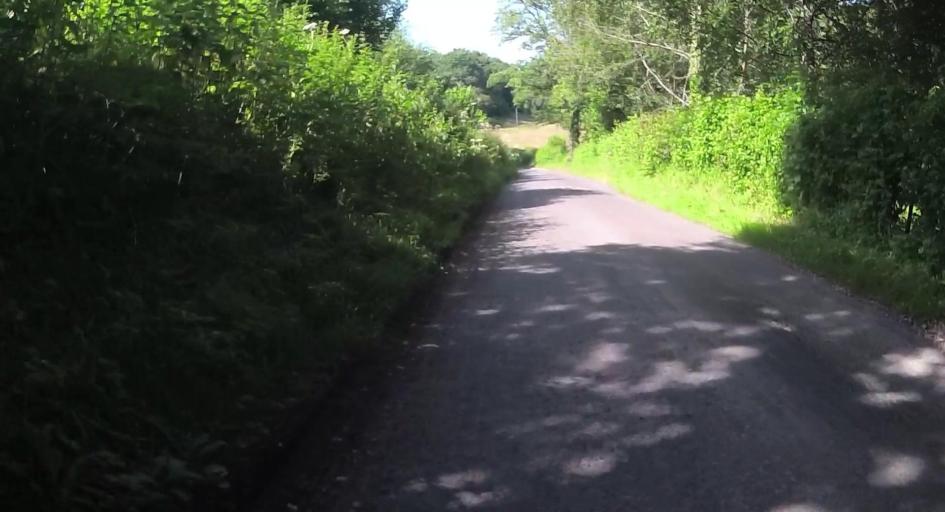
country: GB
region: England
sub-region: Hampshire
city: Kingsley
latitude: 51.1565
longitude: -0.8926
